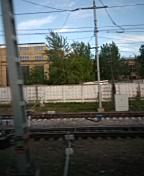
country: RU
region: Moskovskaya
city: Koptevo
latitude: 55.8146
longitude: 37.5074
